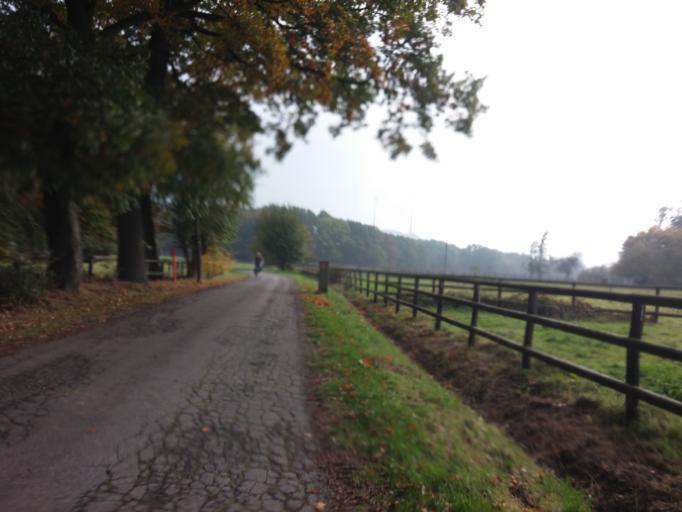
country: DE
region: North Rhine-Westphalia
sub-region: Regierungsbezirk Munster
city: Gladbeck
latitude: 51.6216
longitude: 7.0069
